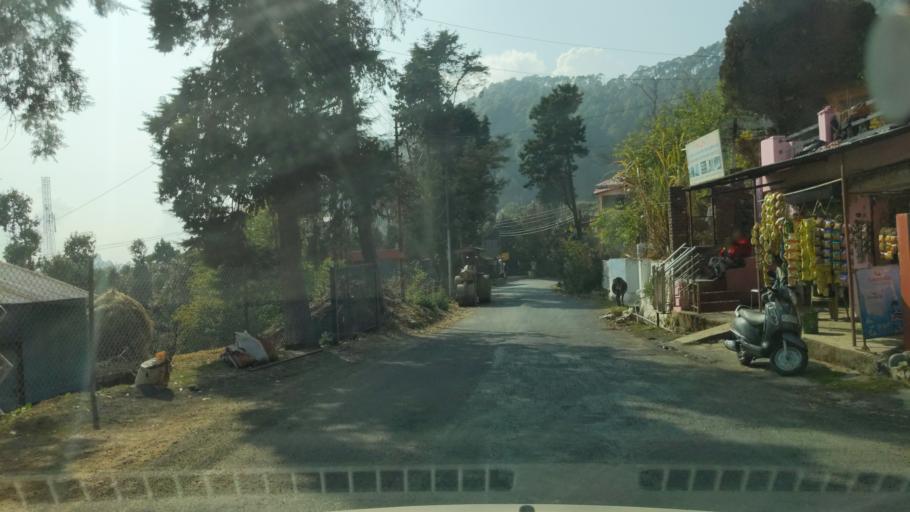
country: IN
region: Uttarakhand
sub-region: Naini Tal
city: Bhowali
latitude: 29.3916
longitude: 79.5325
